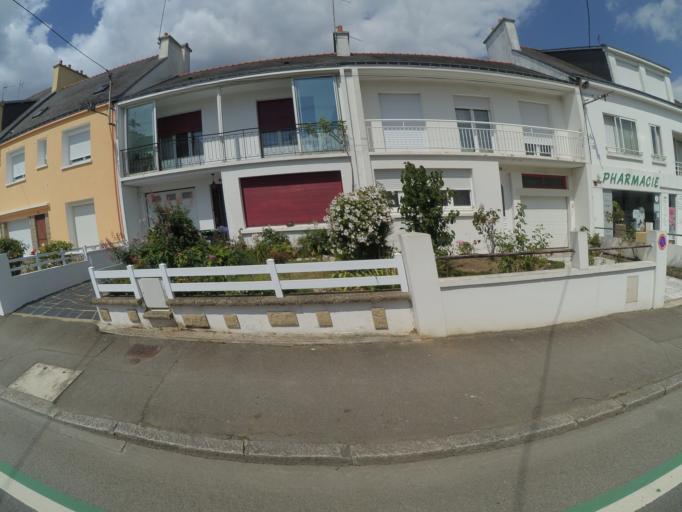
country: FR
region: Brittany
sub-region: Departement du Morbihan
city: Lanester
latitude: 47.7696
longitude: -3.3485
